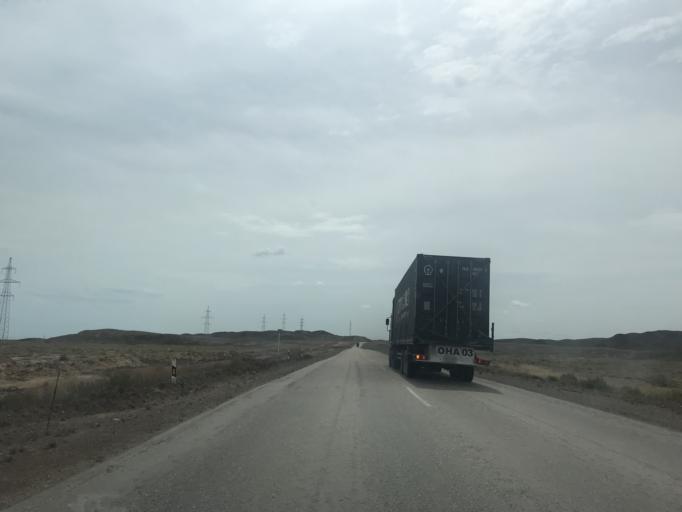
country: KZ
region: Zhambyl
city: Mynaral
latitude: 45.3593
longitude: 73.6754
